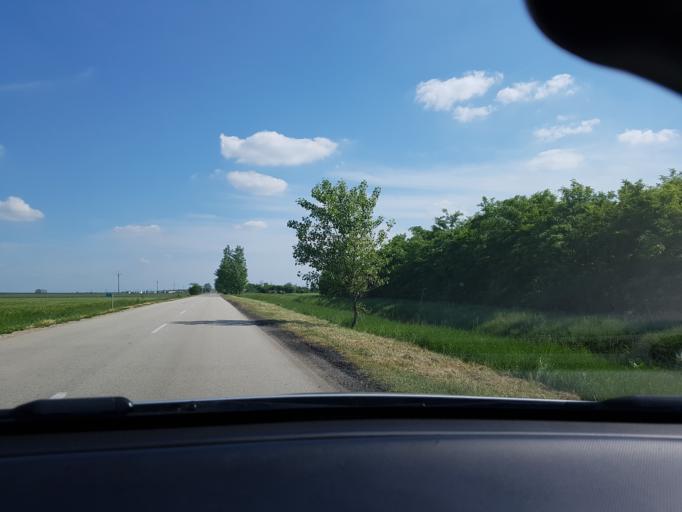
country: HU
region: Csongrad
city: Csanadpalota
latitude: 46.2270
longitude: 20.7090
